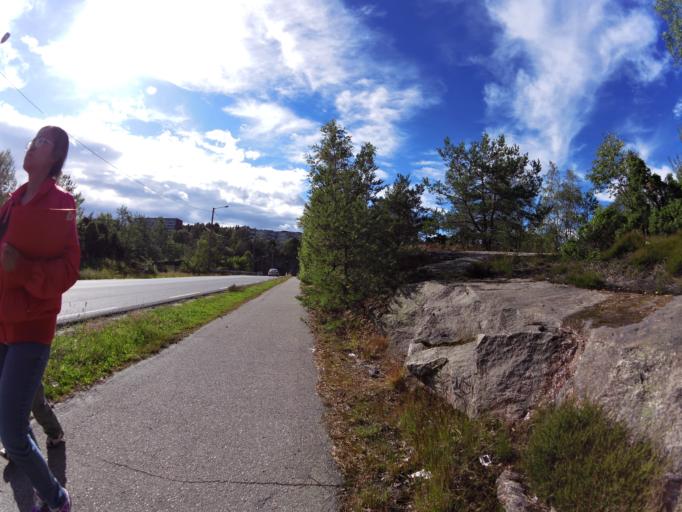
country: NO
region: Ostfold
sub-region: Fredrikstad
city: Fredrikstad
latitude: 59.2597
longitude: 11.0074
